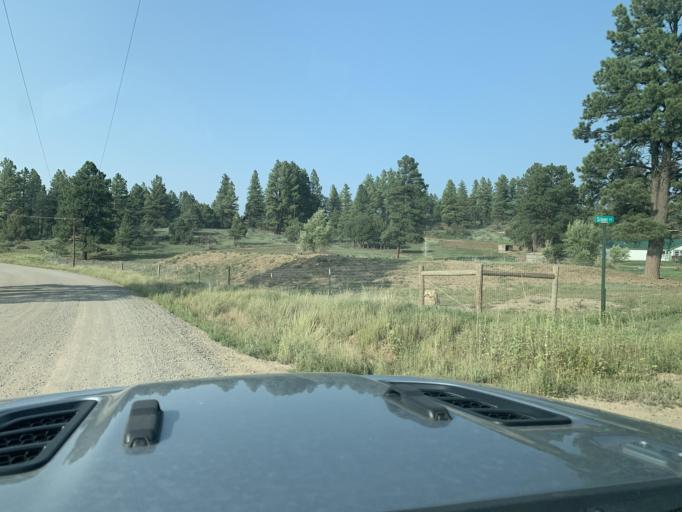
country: US
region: Colorado
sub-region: Archuleta County
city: Pagosa Springs
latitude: 37.2200
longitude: -107.2101
